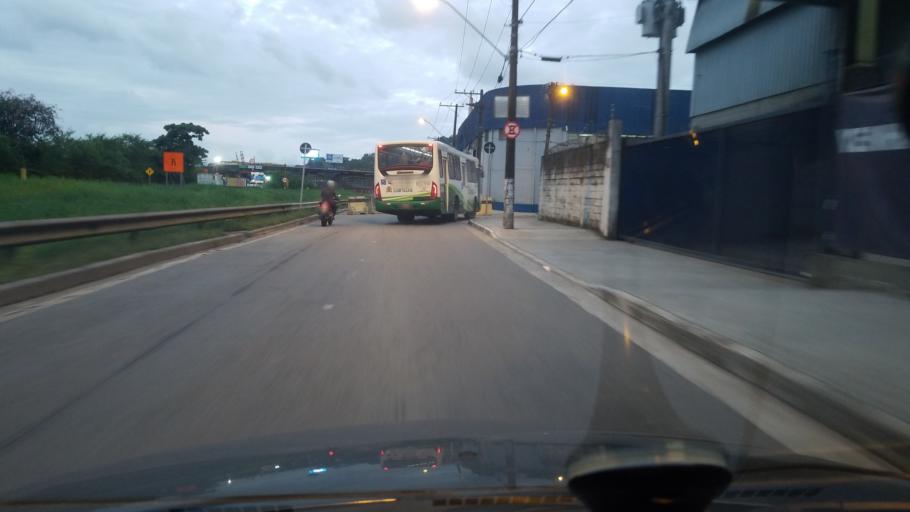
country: BR
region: Sao Paulo
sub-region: Santos
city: Santos
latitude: -23.9302
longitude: -46.3582
